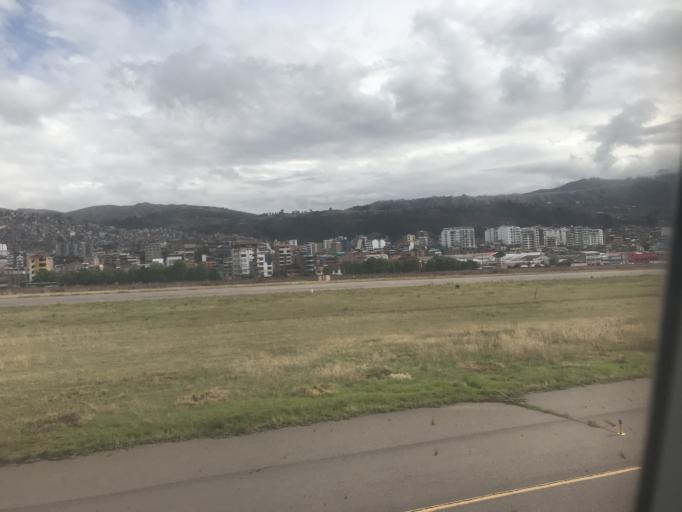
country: PE
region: Cusco
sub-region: Provincia de Cusco
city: Cusco
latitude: -13.5356
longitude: -71.9536
